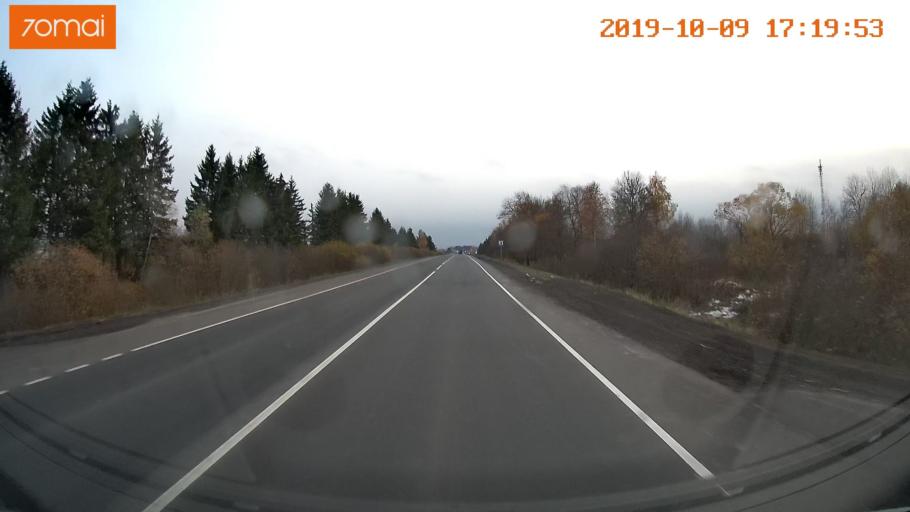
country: RU
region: Ivanovo
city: Furmanov
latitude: 57.2408
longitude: 41.1476
